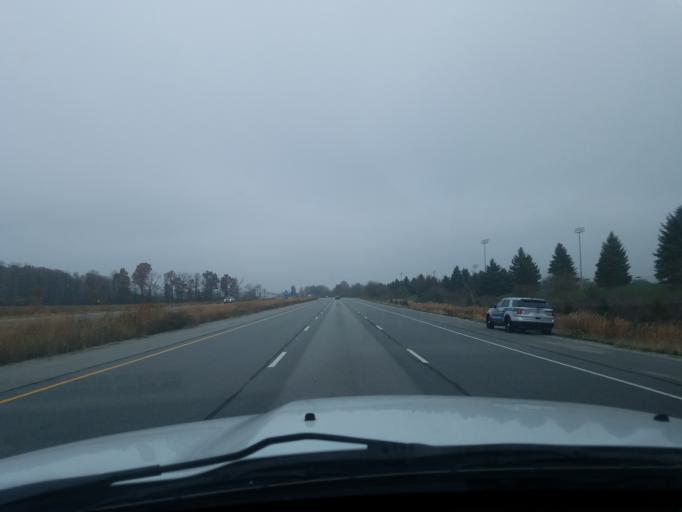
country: US
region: Indiana
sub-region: Hamilton County
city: Westfield
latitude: 40.0547
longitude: -86.1315
